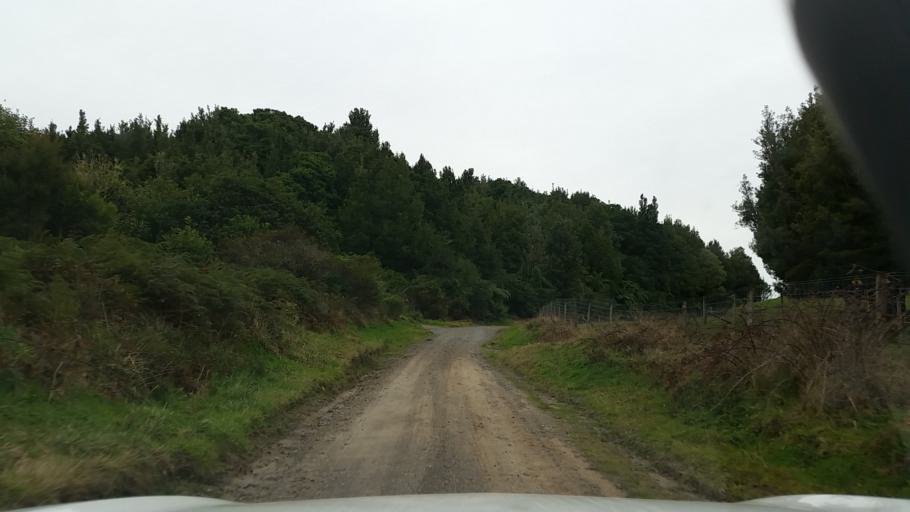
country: NZ
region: Bay of Plenty
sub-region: Rotorua District
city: Rotorua
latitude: -38.1573
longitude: 176.3720
